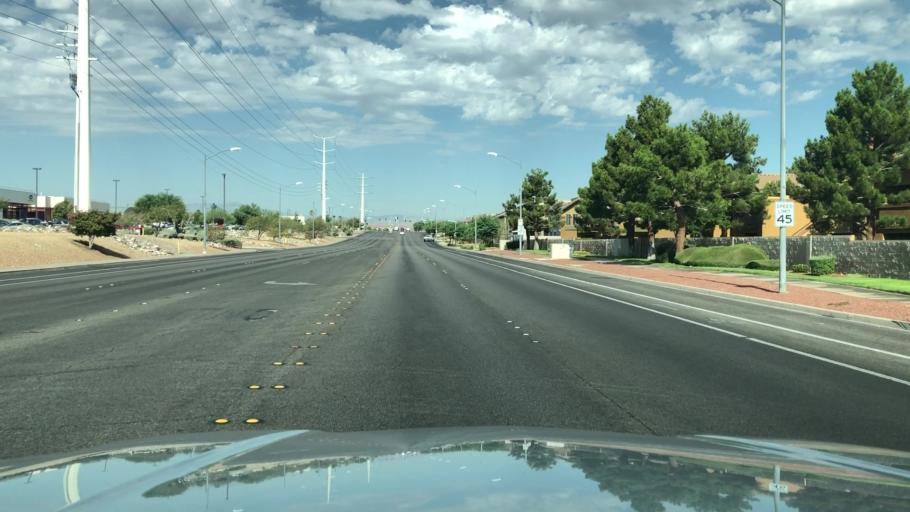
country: US
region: Nevada
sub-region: Clark County
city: Whitney
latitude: 36.0418
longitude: -115.0412
